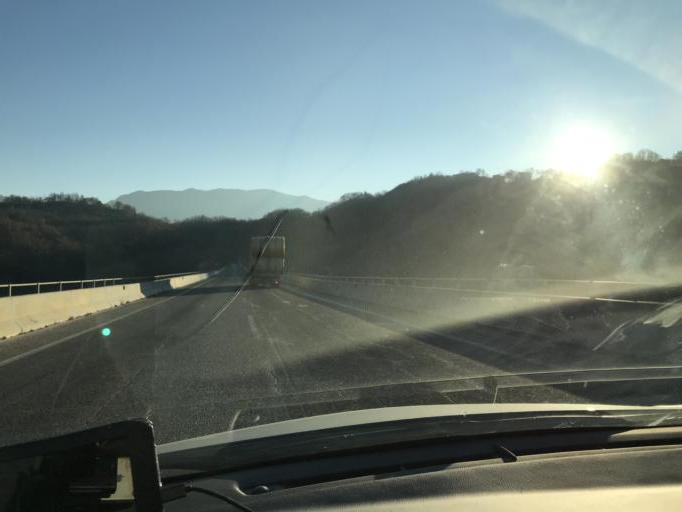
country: IT
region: Latium
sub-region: Provincia di Rieti
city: Fiamignano
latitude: 42.2546
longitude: 13.1408
